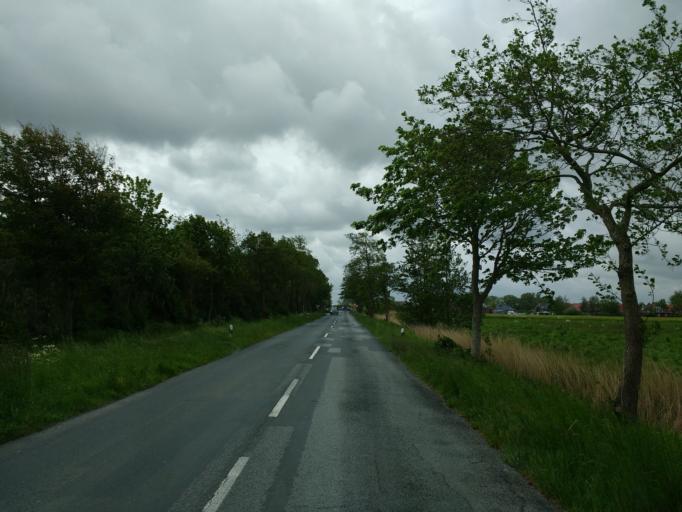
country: DE
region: Lower Saxony
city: Schillig
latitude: 53.6889
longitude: 8.0088
